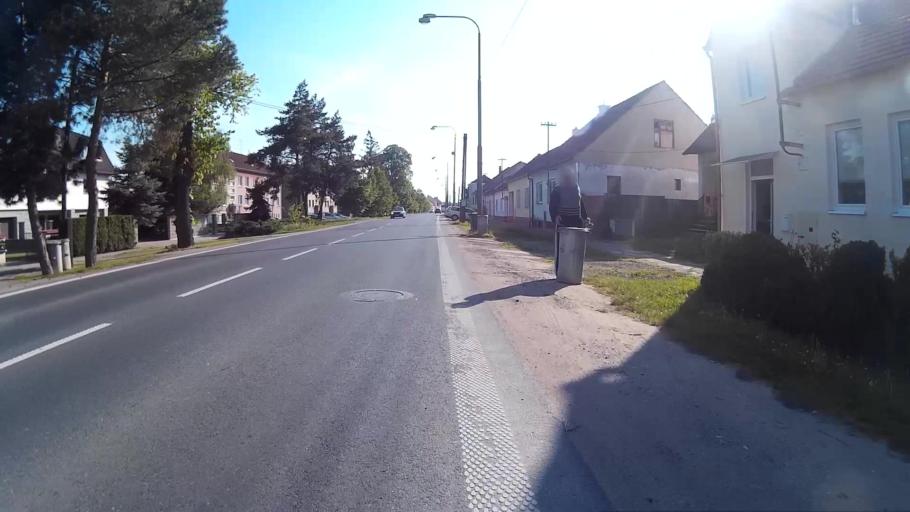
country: CZ
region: South Moravian
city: Pohorelice
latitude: 48.9872
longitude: 16.5346
